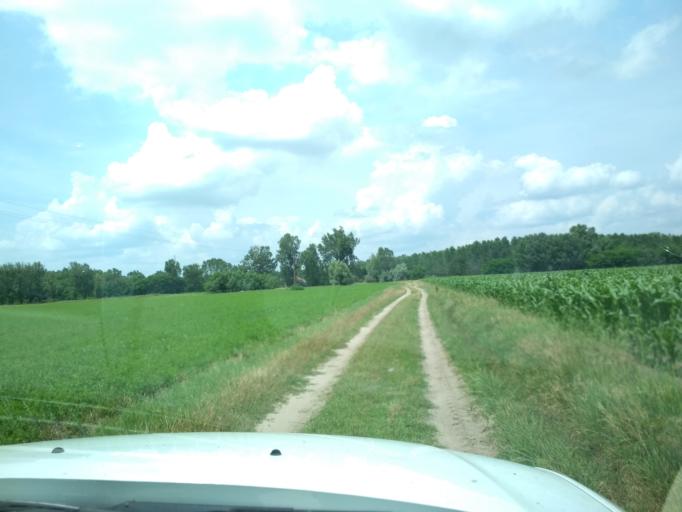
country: HU
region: Pest
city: Nagykata
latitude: 47.3892
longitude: 19.7853
